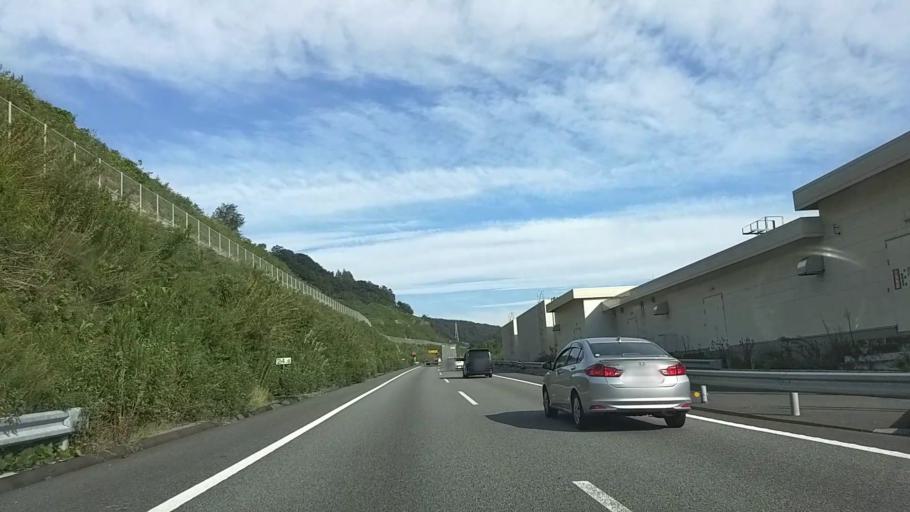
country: JP
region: Kanagawa
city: Zama
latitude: 35.5380
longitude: 139.3244
